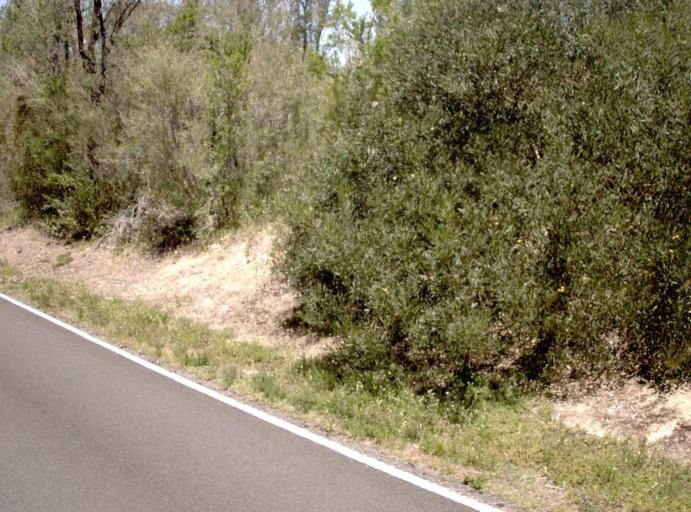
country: AU
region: Victoria
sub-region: Latrobe
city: Morwell
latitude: -38.8692
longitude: 146.2639
